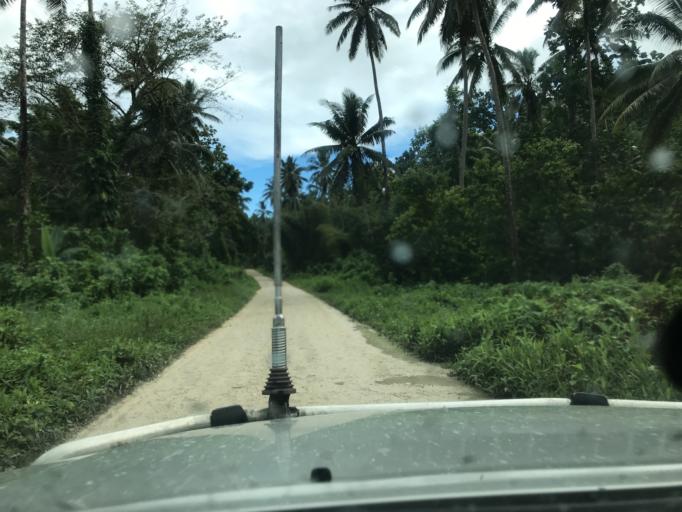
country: SB
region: Malaita
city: Auki
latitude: -8.4243
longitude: 160.6229
